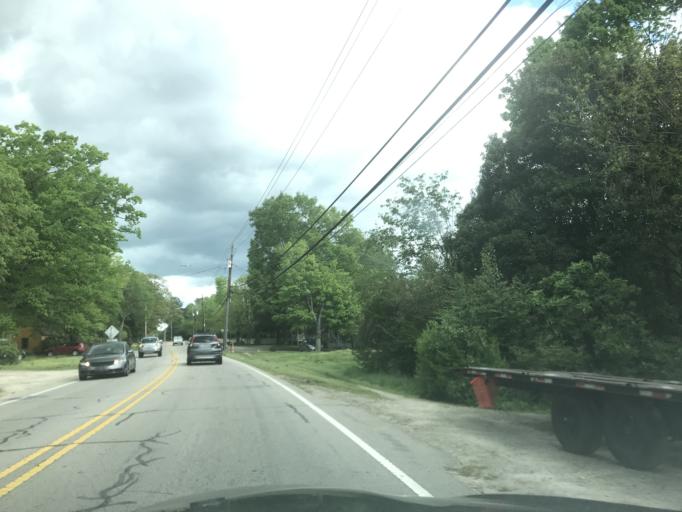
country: US
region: North Carolina
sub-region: Wake County
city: West Raleigh
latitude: 35.7803
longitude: -78.7211
